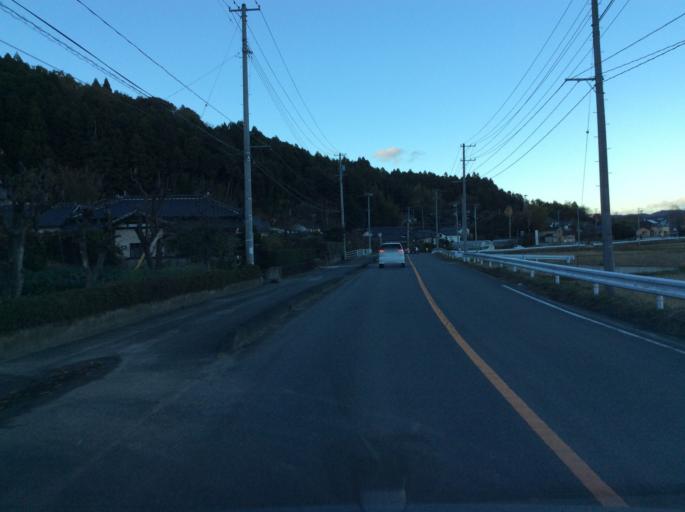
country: JP
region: Fukushima
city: Iwaki
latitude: 37.0717
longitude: 140.8707
